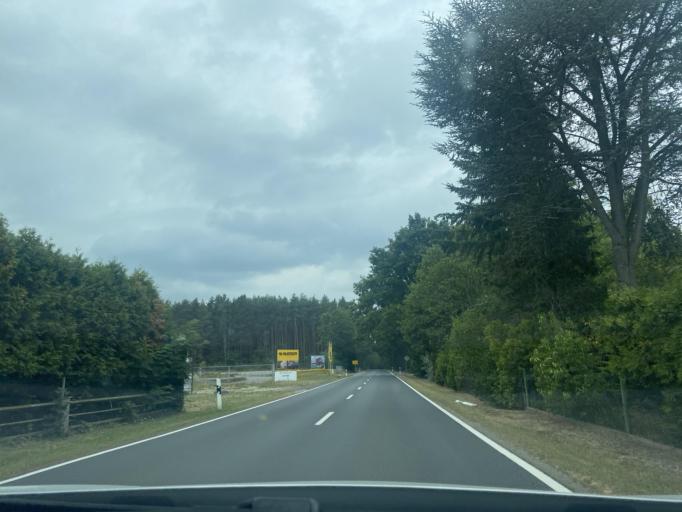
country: DE
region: Saxony
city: Guttau
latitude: 51.2757
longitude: 14.6296
